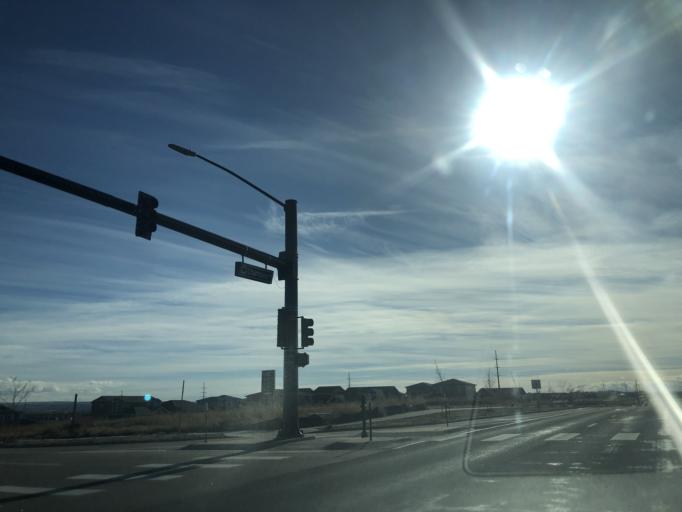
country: US
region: Colorado
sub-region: Douglas County
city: Stonegate
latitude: 39.5563
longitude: -104.8070
